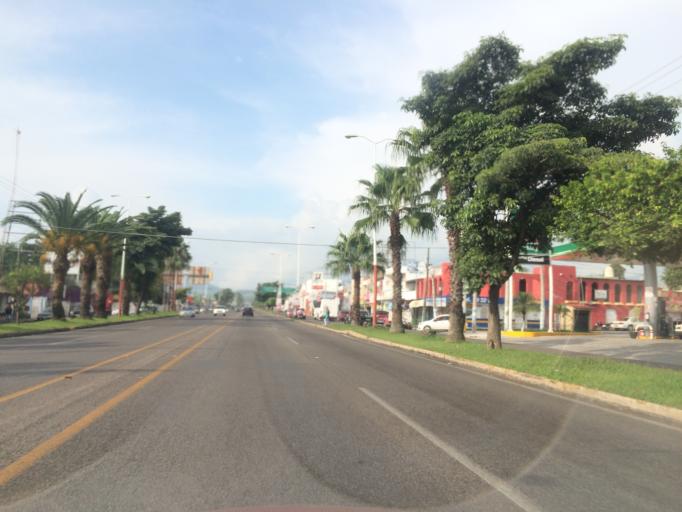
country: MX
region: Nayarit
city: Xalisco
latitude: 21.4606
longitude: -104.8924
